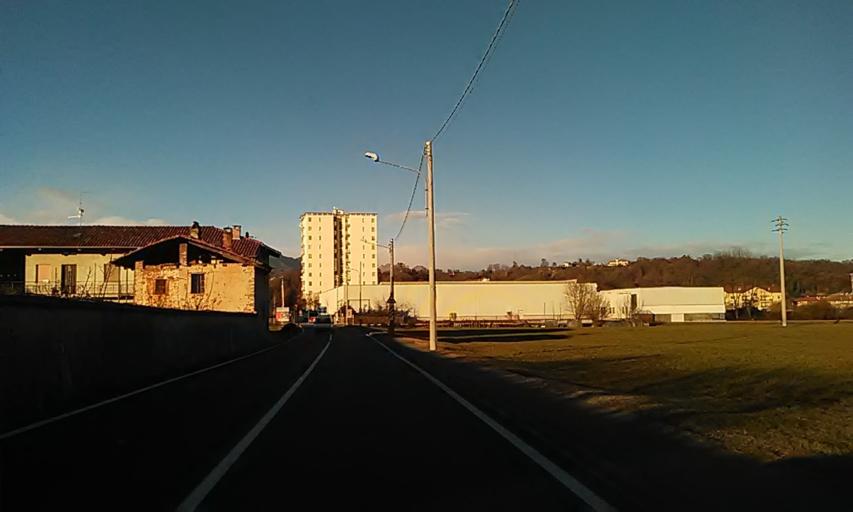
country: IT
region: Piedmont
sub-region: Provincia di Biella
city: Valdengo
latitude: 45.5605
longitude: 8.1405
